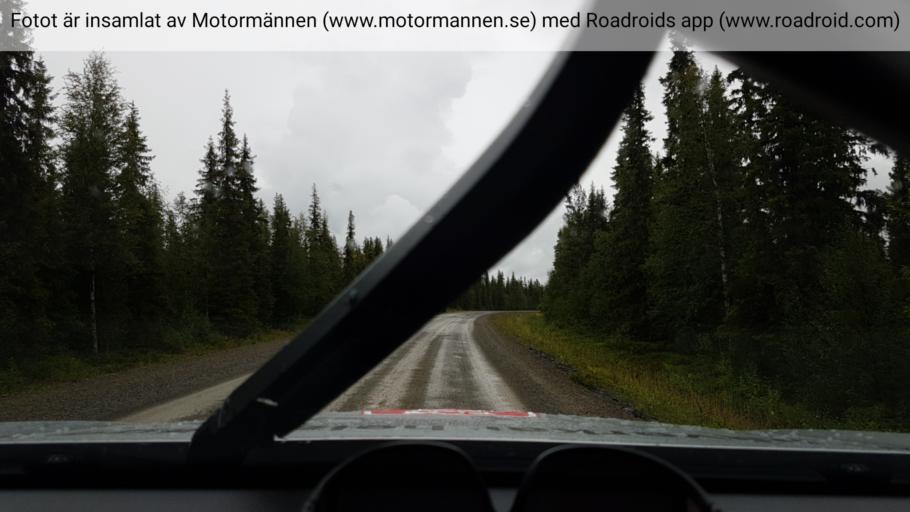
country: SE
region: Vaesterbotten
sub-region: Asele Kommun
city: Insjon
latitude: 64.8050
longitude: 17.5525
